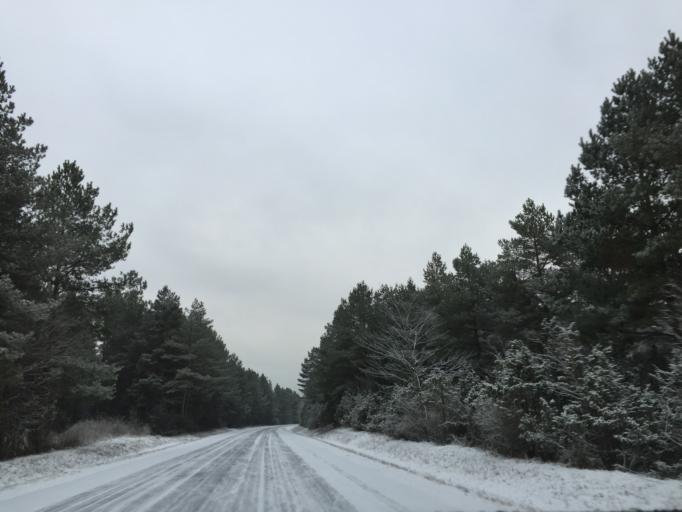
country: EE
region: Saare
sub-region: Orissaare vald
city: Orissaare
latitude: 58.6236
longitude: 23.3140
